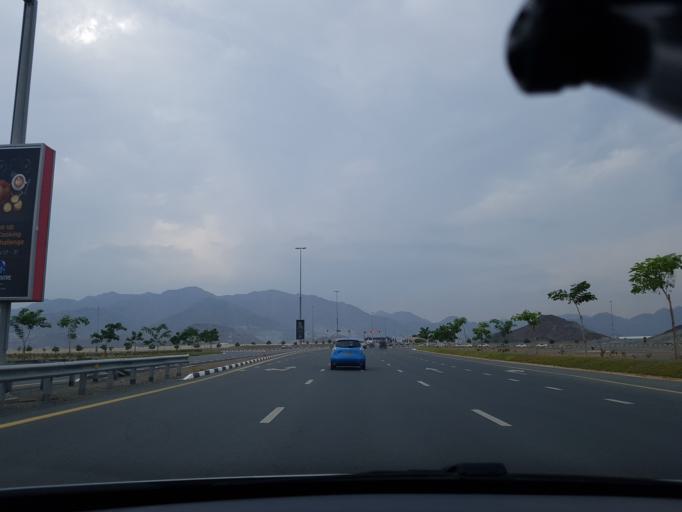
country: AE
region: Al Fujayrah
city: Al Fujayrah
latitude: 25.1229
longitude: 56.2846
